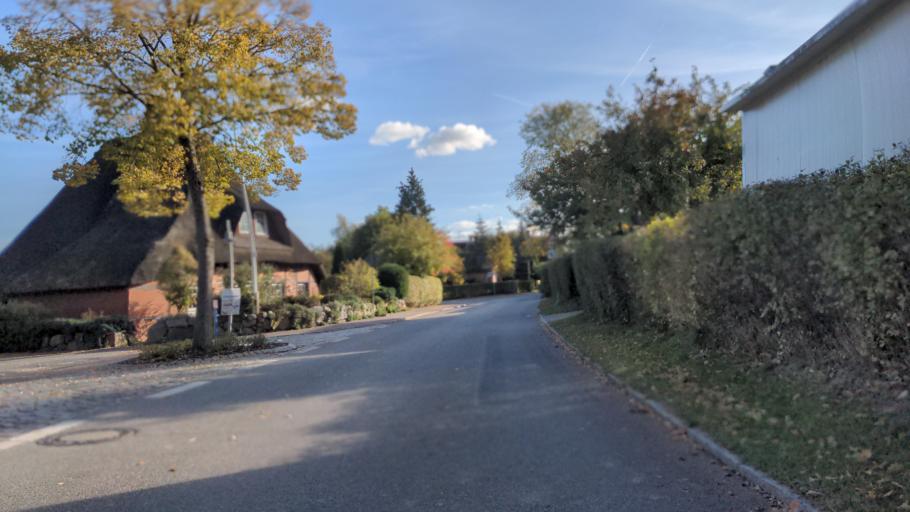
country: DE
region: Schleswig-Holstein
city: Manhagen
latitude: 54.1957
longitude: 10.9139
